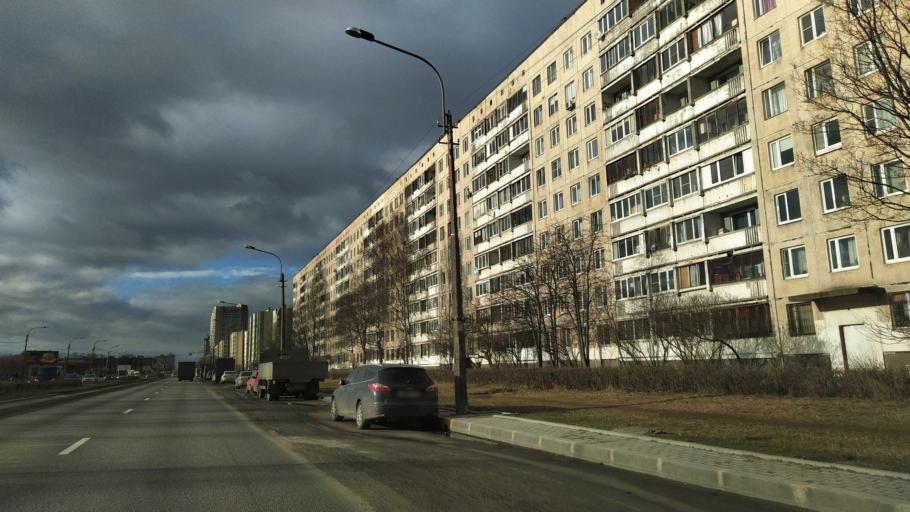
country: RU
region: St.-Petersburg
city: Grazhdanka
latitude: 60.0316
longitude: 30.3890
